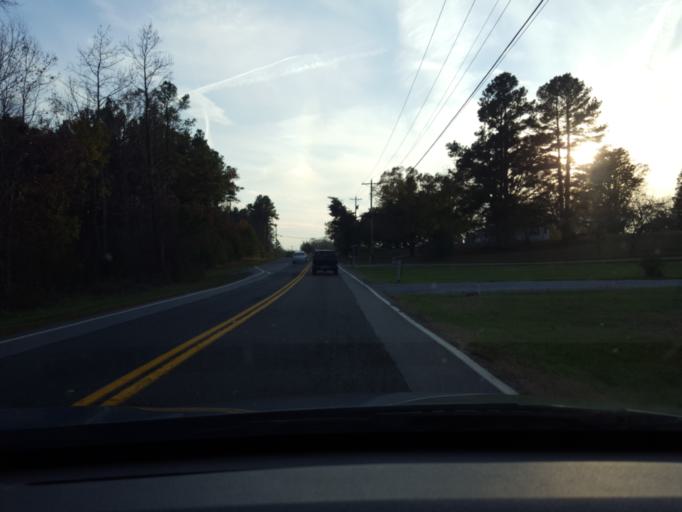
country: US
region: Maryland
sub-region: Charles County
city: Hughesville
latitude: 38.5092
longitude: -76.8620
